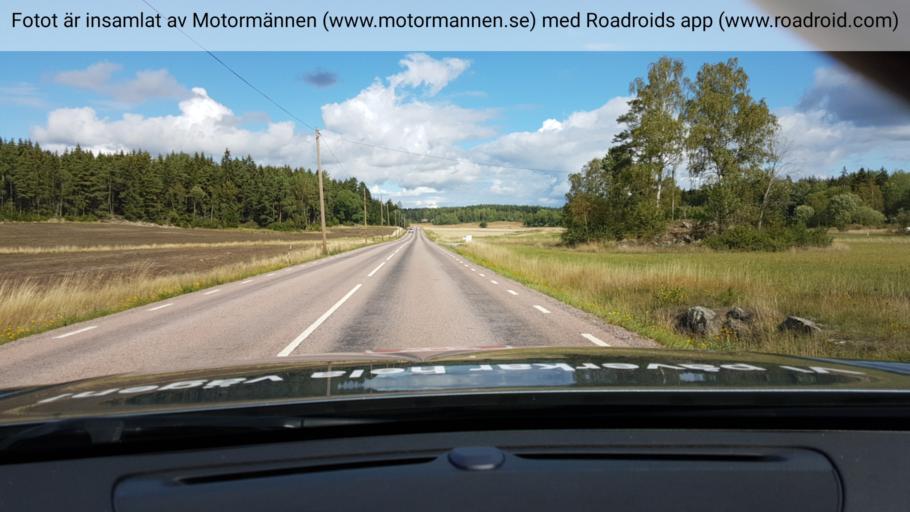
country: SE
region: Soedermanland
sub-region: Strangnas Kommun
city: Mariefred
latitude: 59.2812
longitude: 17.2242
